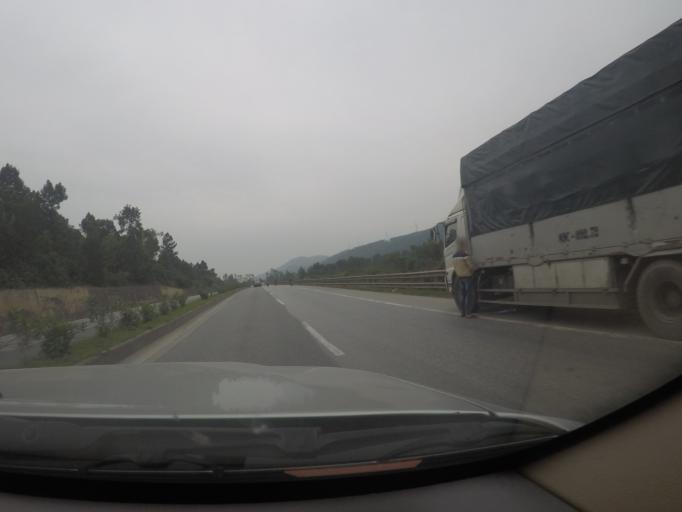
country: VN
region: Nghe An
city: Dien Chau
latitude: 18.8818
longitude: 105.6031
